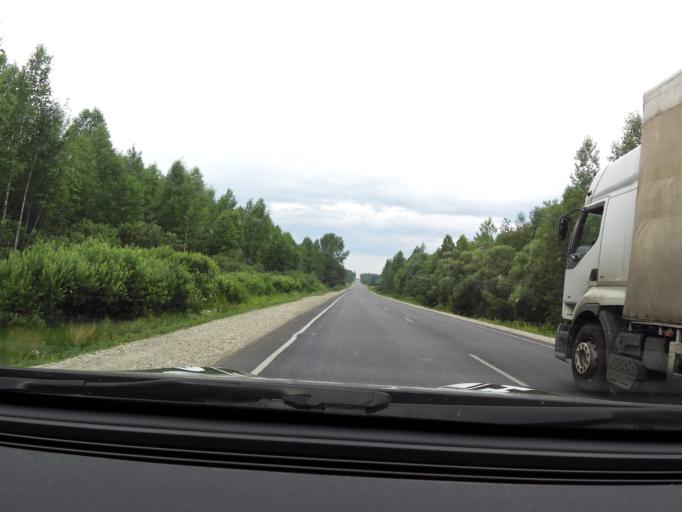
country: RU
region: Bashkortostan
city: Ulu-Telyak
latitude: 54.8467
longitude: 57.0995
